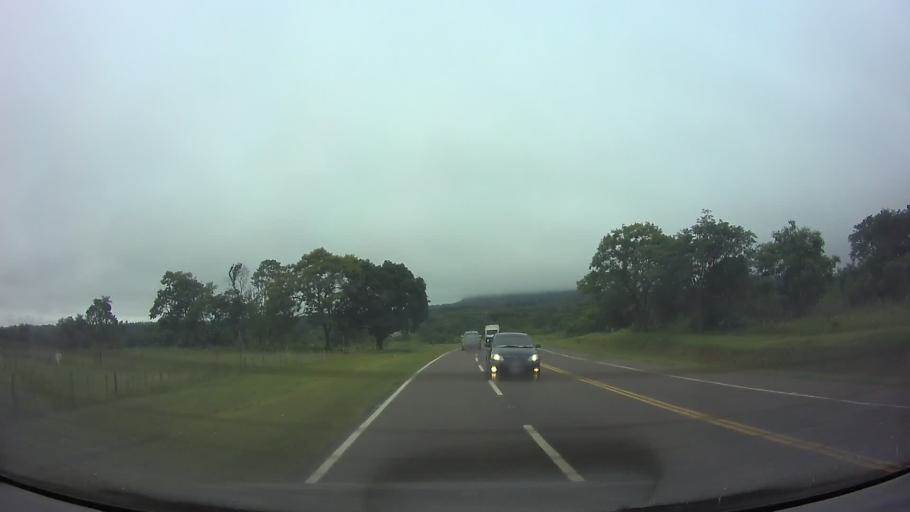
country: PY
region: Paraguari
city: Paraguari
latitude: -25.6098
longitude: -57.1851
